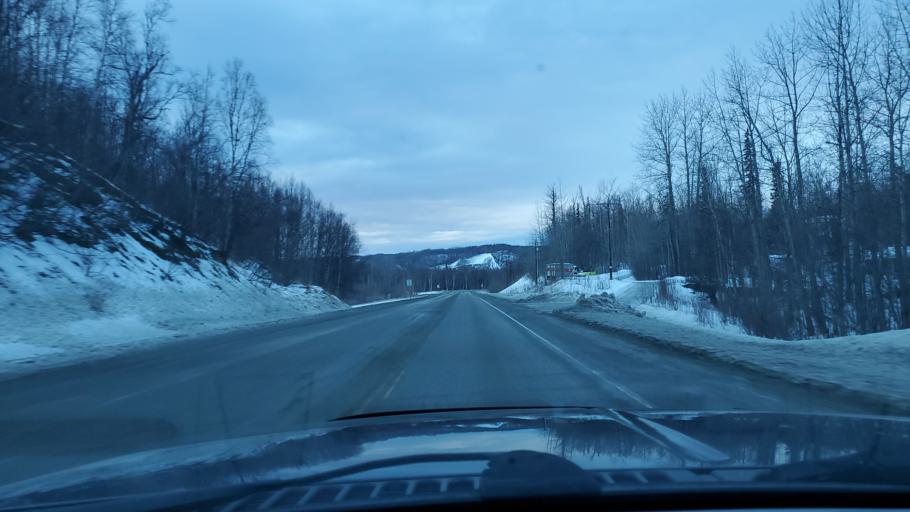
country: US
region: Alaska
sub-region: Matanuska-Susitna Borough
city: Lazy Mountain
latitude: 61.6776
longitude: -149.0156
